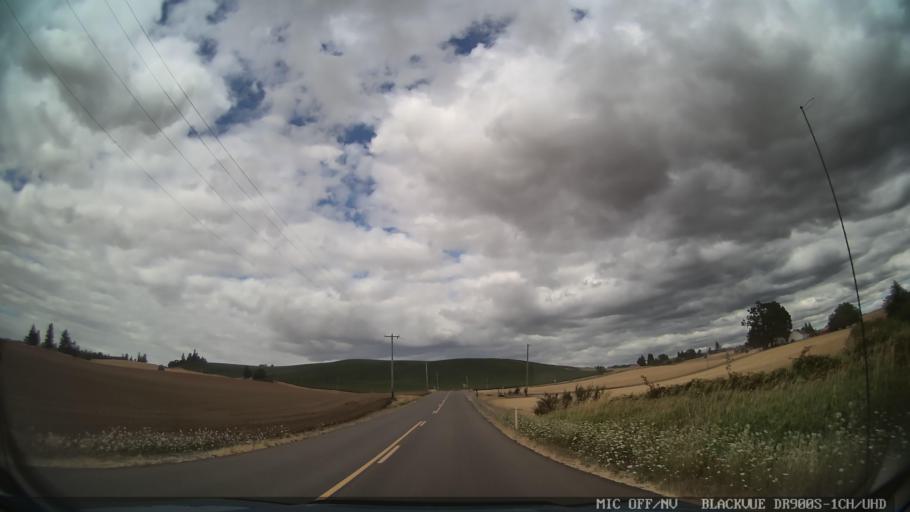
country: US
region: Oregon
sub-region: Marion County
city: Sublimity
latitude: 44.8701
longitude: -122.7366
